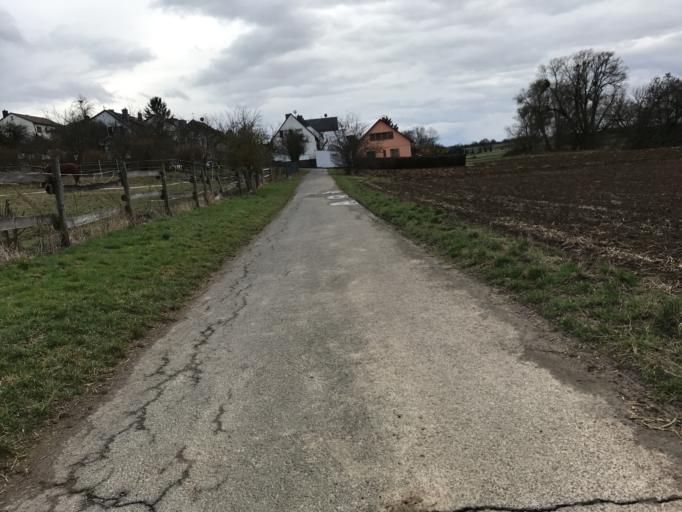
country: DE
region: Hesse
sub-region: Regierungsbezirk Darmstadt
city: Niedernhausen
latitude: 50.0851
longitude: 8.3225
